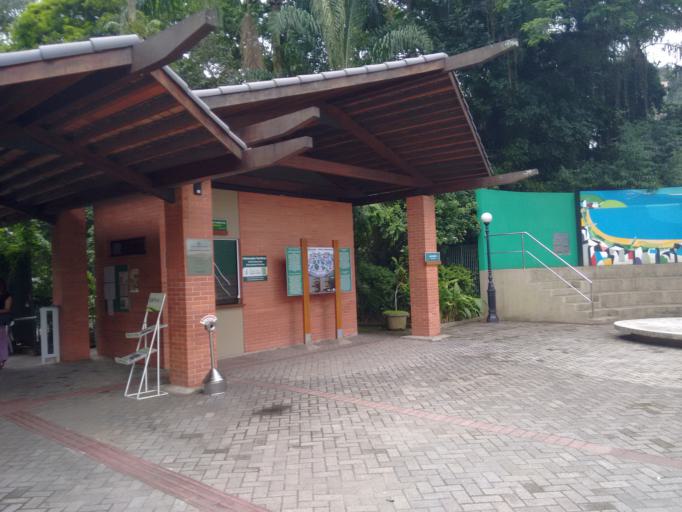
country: BR
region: Sao Paulo
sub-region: Santos
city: Santos
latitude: -23.9654
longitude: -46.3490
